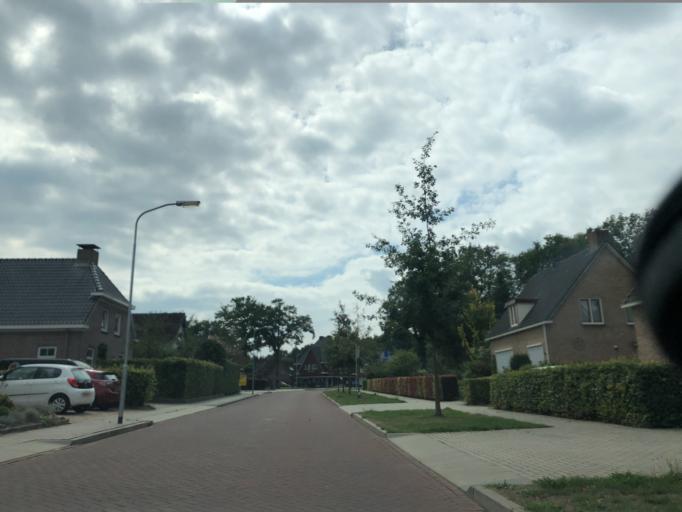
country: NL
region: Drenthe
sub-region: Gemeente Borger-Odoorn
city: Borger
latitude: 52.9193
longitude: 6.7949
